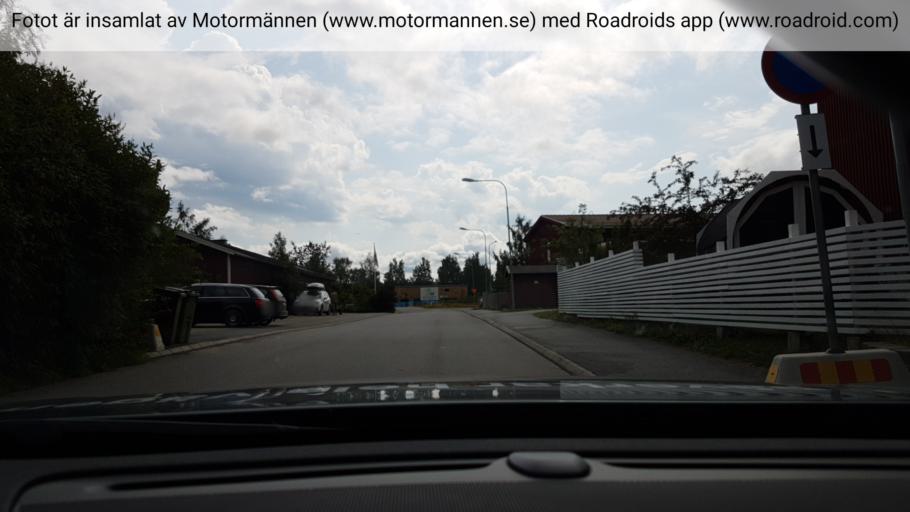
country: SE
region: Vaesterbotten
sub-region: Umea Kommun
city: Umea
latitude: 63.8234
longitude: 20.2319
